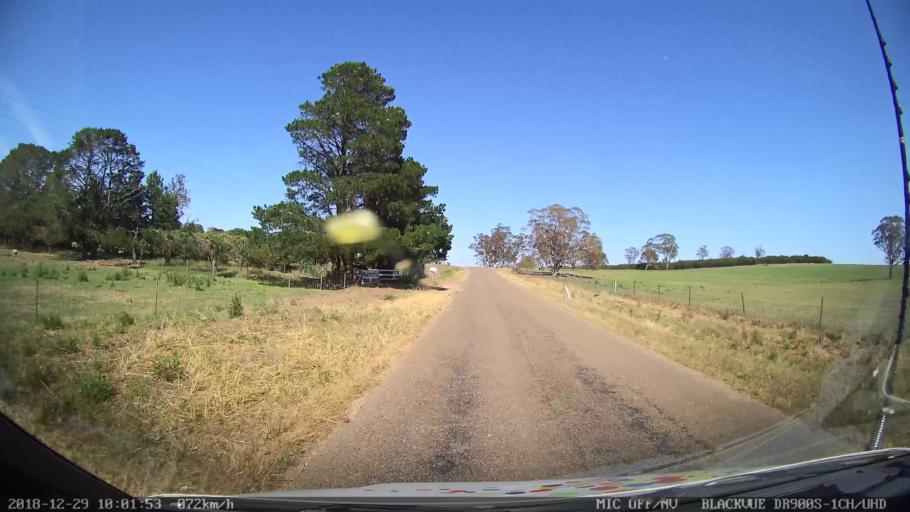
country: AU
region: New South Wales
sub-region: Goulburn Mulwaree
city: Goulburn
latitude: -34.8006
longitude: 149.4711
